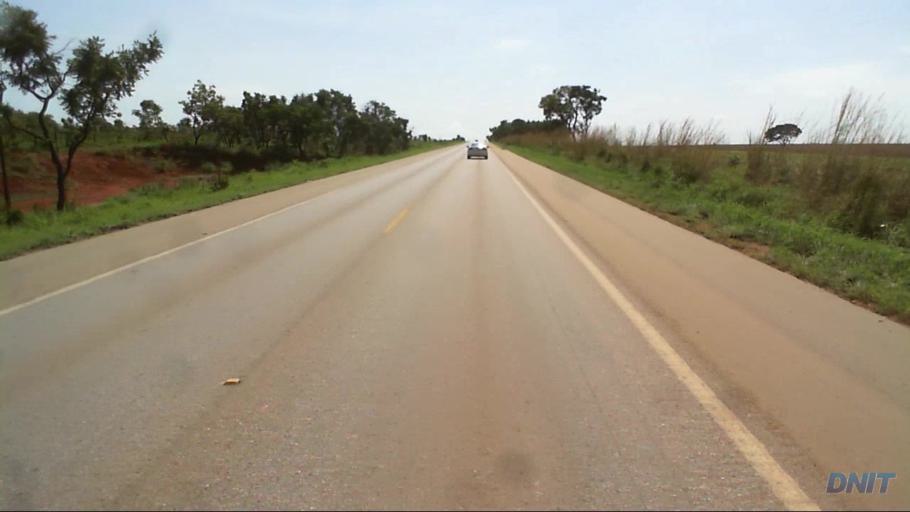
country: BR
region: Goias
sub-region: Barro Alto
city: Barro Alto
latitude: -15.2028
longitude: -48.7488
